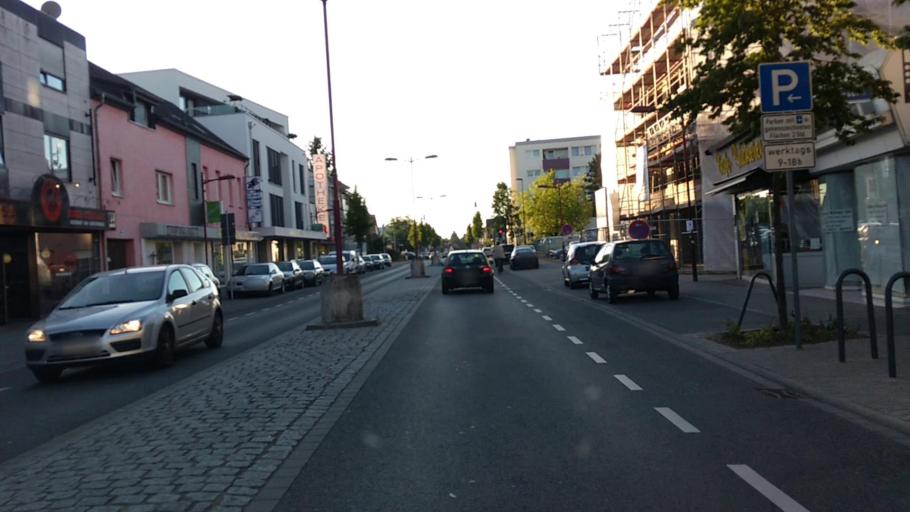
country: DE
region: North Rhine-Westphalia
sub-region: Regierungsbezirk Koln
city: Kerpen
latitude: 50.9042
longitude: 6.6761
